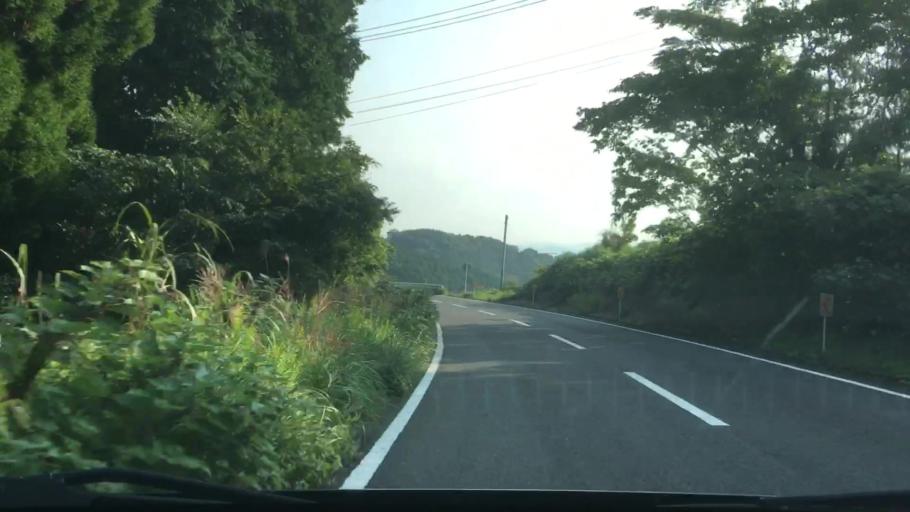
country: JP
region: Nagasaki
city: Sasebo
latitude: 33.0397
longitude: 129.6944
